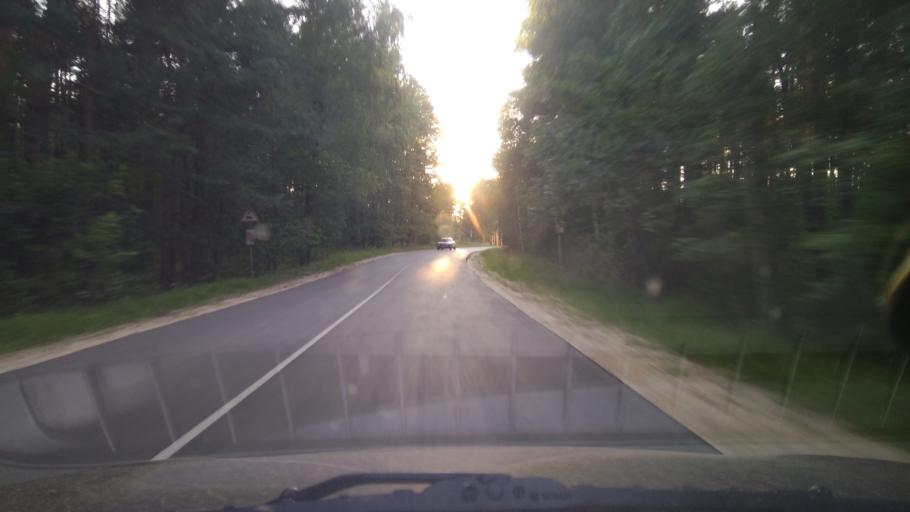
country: BY
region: Brest
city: Nyakhachava
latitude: 52.6025
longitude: 25.0891
